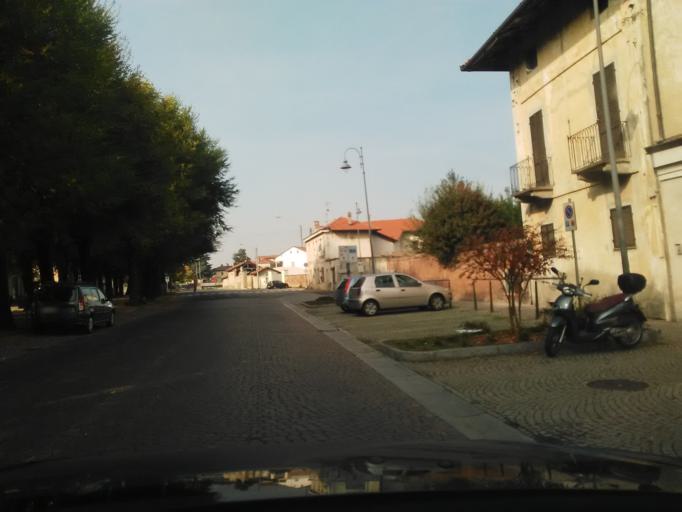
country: IT
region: Piedmont
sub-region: Provincia di Vercelli
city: Tronzano Vercellese
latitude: 45.3426
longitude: 8.1718
